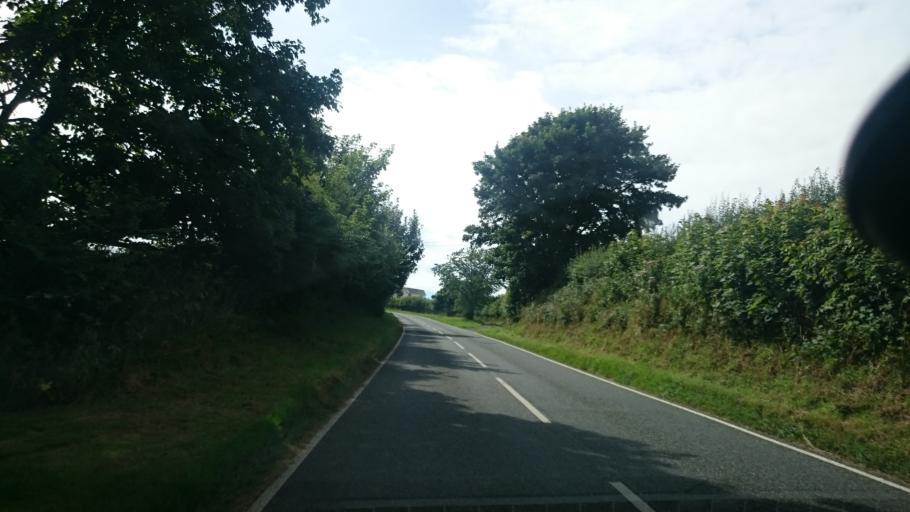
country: GB
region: Wales
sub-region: Pembrokeshire
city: Hook
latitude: 51.7540
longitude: -4.9341
